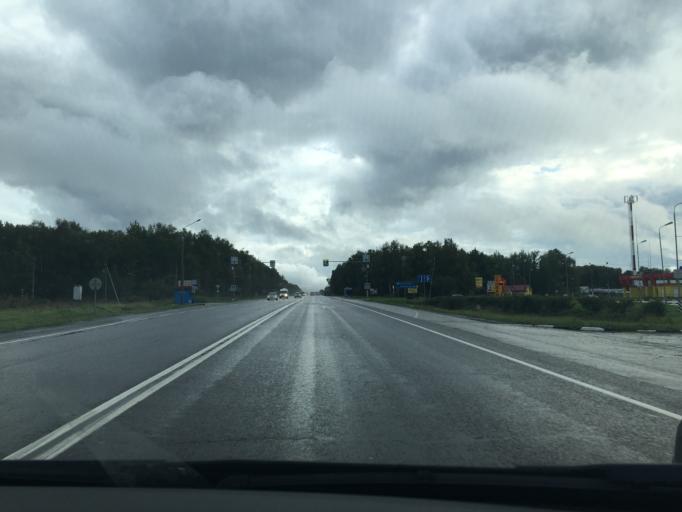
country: RU
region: Kaluga
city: Balabanovo
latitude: 55.1496
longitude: 36.6618
